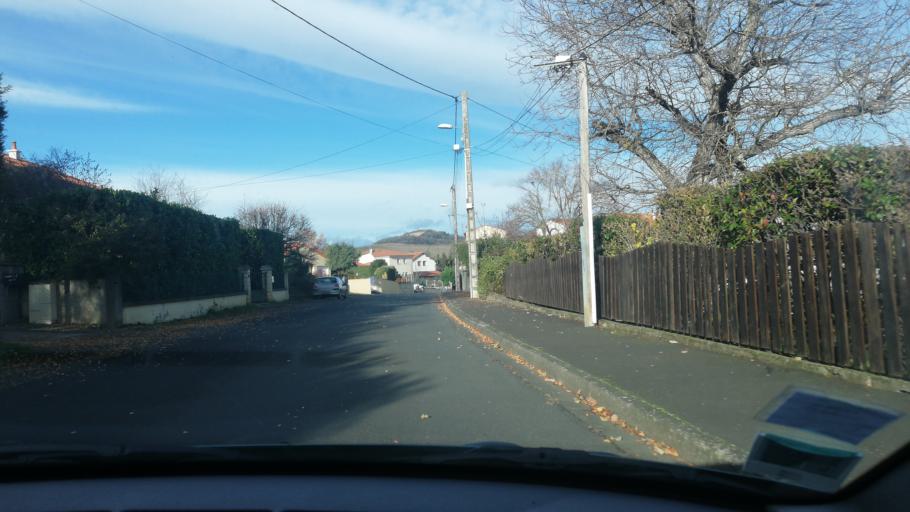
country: FR
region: Auvergne
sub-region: Departement du Puy-de-Dome
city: Billom
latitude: 45.7175
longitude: 3.3420
